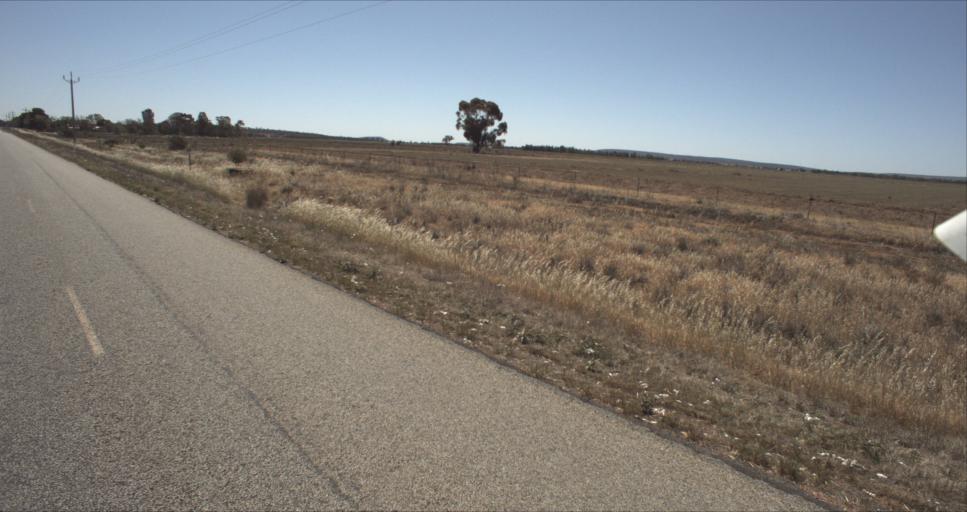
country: AU
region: New South Wales
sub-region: Leeton
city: Leeton
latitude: -34.4456
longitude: 146.2970
